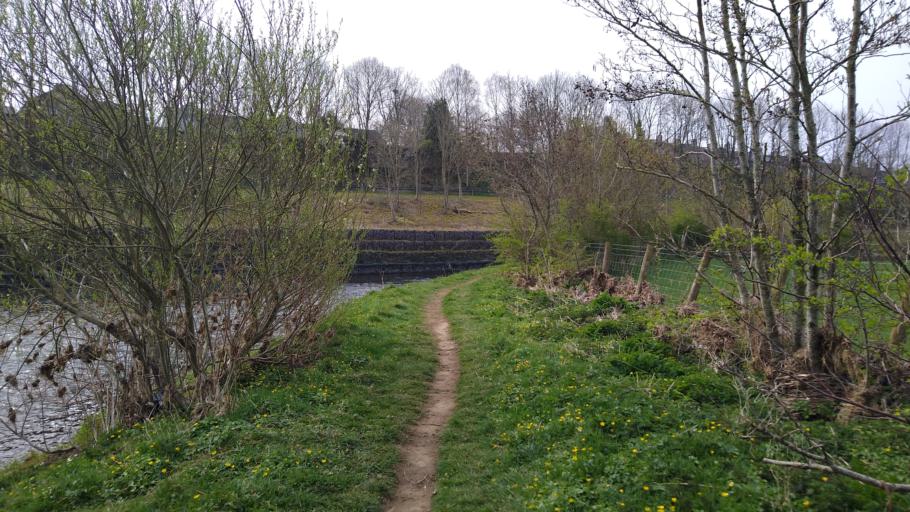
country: GB
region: England
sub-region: Cumbria
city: Dearham
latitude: 54.6600
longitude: -3.4355
